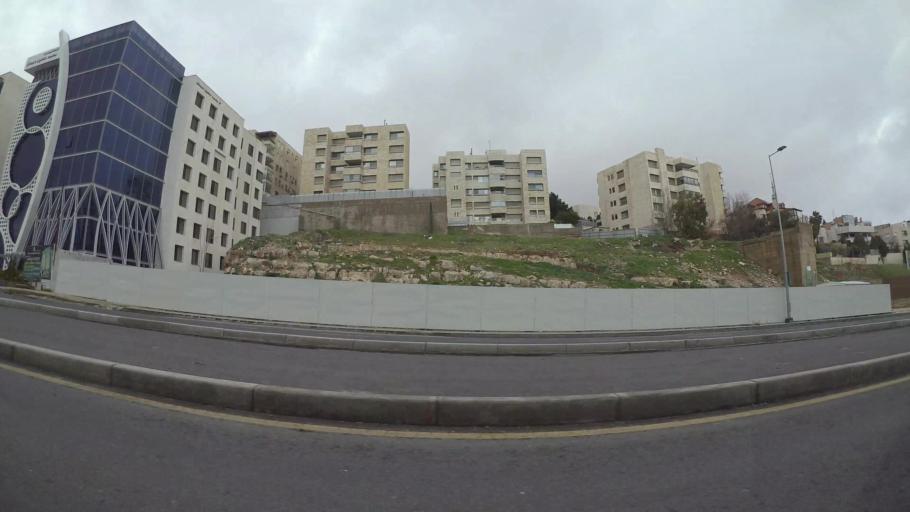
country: JO
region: Amman
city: Amman
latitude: 31.9547
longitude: 35.8854
